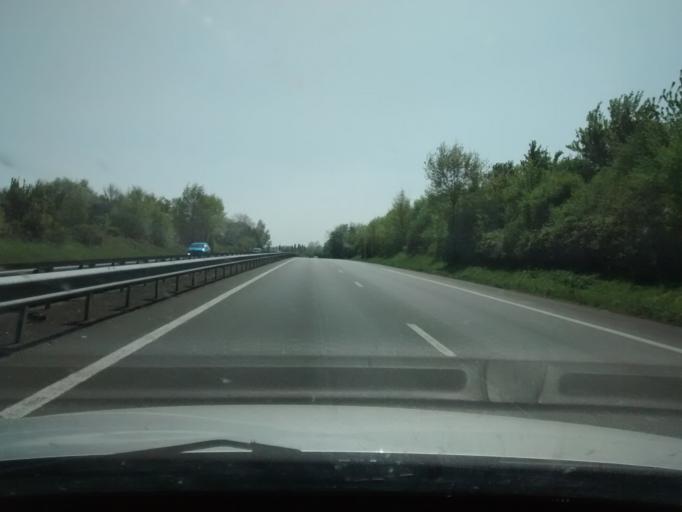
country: FR
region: Pays de la Loire
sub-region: Departement de la Sarthe
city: Coulaines
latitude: 48.0314
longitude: 0.2146
